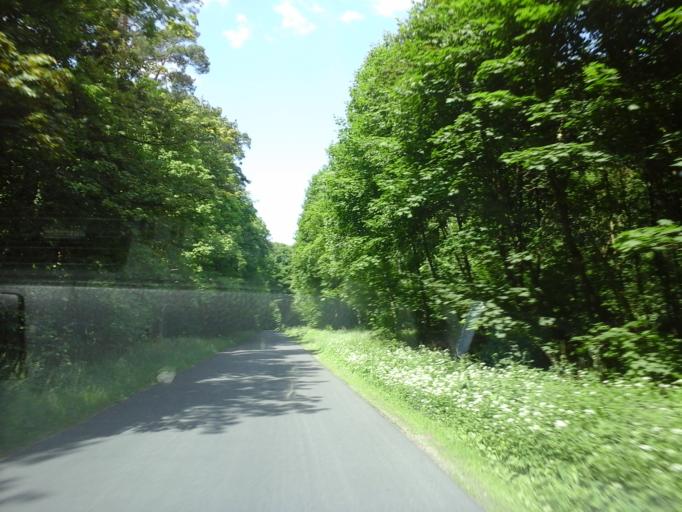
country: PL
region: West Pomeranian Voivodeship
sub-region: Powiat choszczenski
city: Bierzwnik
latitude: 53.1560
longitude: 15.6265
